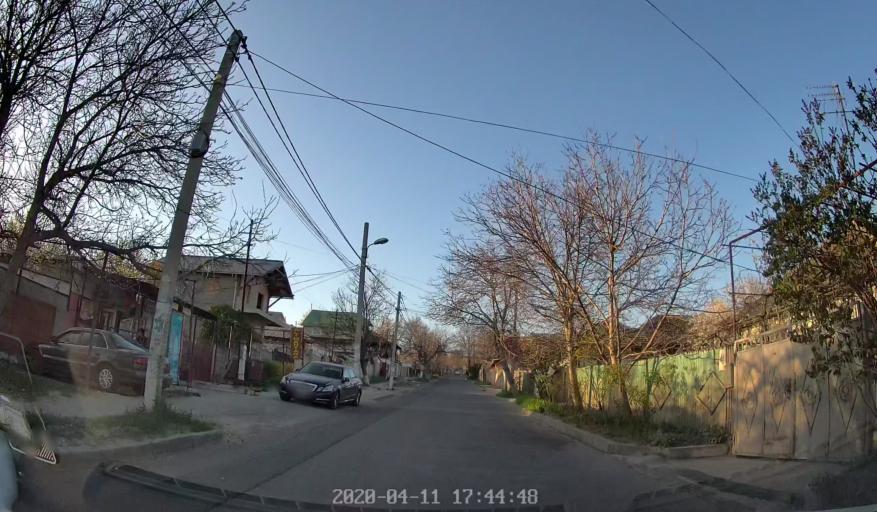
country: MD
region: Chisinau
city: Chisinau
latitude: 46.9801
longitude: 28.8234
